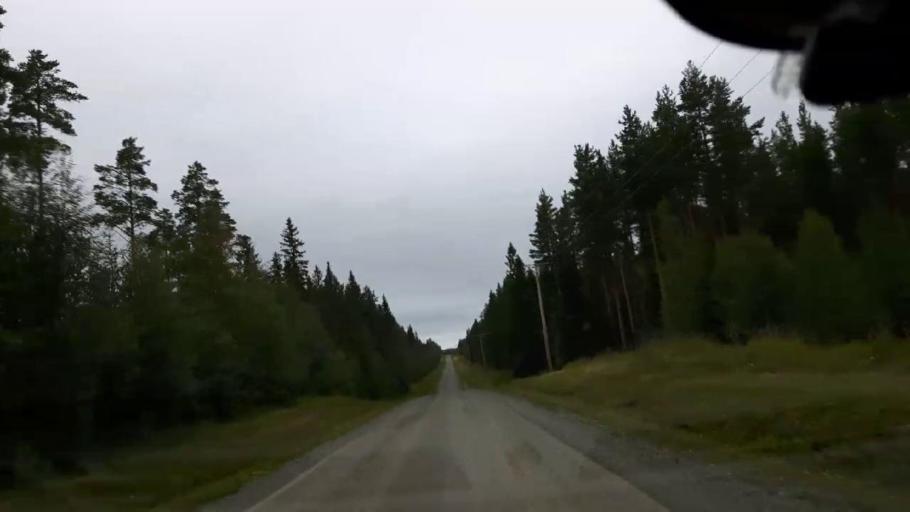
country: SE
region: Vaesternorrland
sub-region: Ange Kommun
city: Fransta
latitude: 62.8003
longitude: 16.0246
